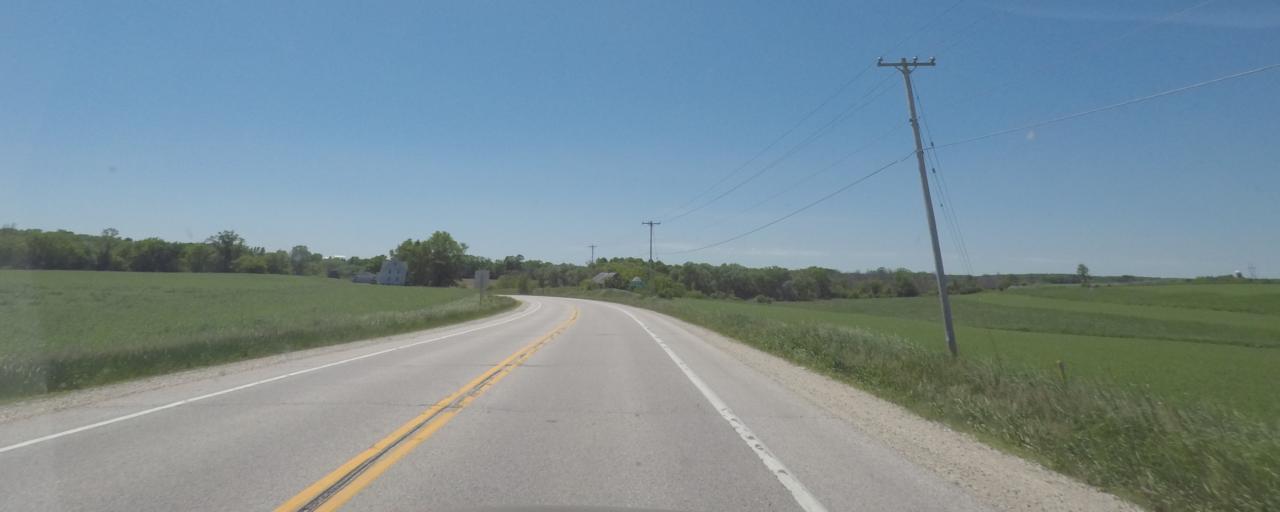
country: US
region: Wisconsin
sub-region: Ozaukee County
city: Kohler
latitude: 43.5555
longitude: -88.0760
